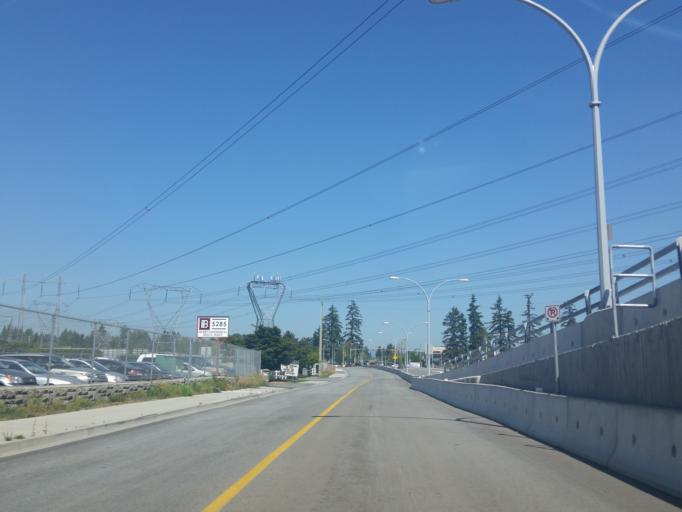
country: CA
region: British Columbia
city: Langley
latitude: 49.0985
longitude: -122.6913
